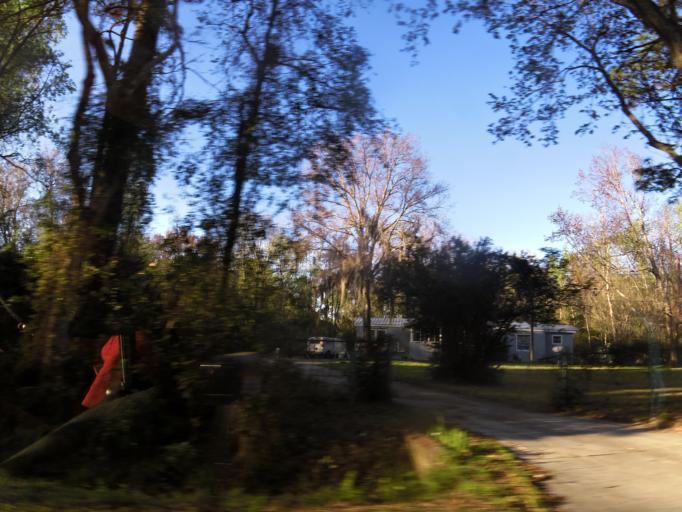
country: US
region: Florida
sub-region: Duval County
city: Jacksonville
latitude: 30.4625
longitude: -81.6450
